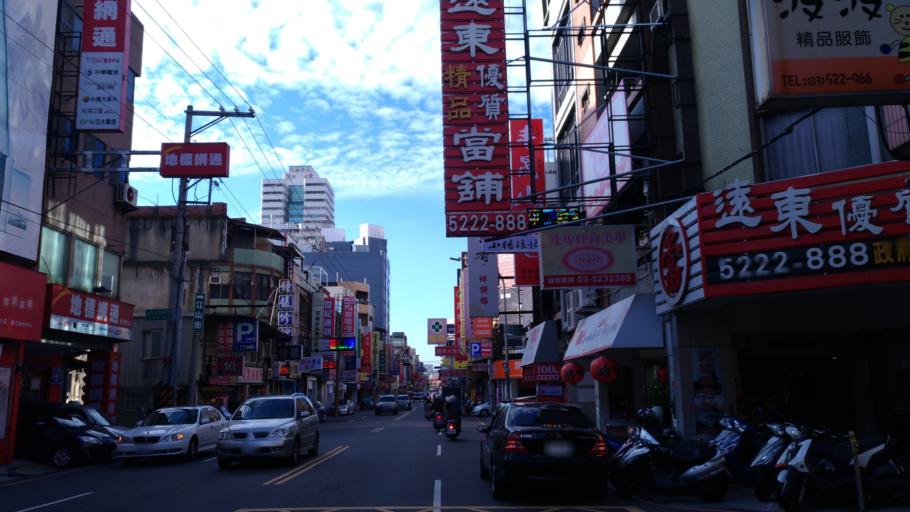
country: TW
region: Taiwan
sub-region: Hsinchu
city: Hsinchu
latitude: 24.8043
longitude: 120.9639
